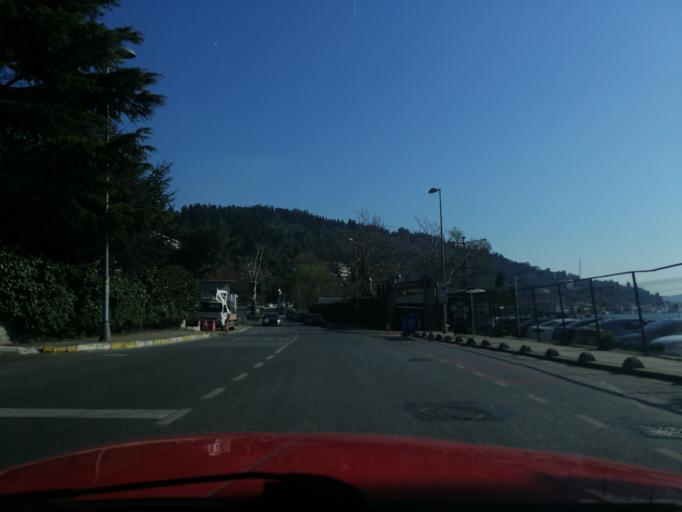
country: TR
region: Istanbul
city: UEskuedar
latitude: 41.0699
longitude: 29.0568
